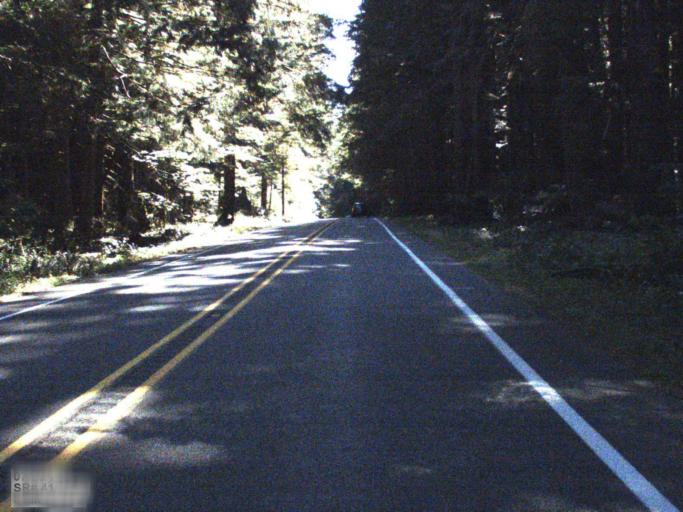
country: US
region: Washington
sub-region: King County
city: Enumclaw
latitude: 47.1533
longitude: -121.6851
